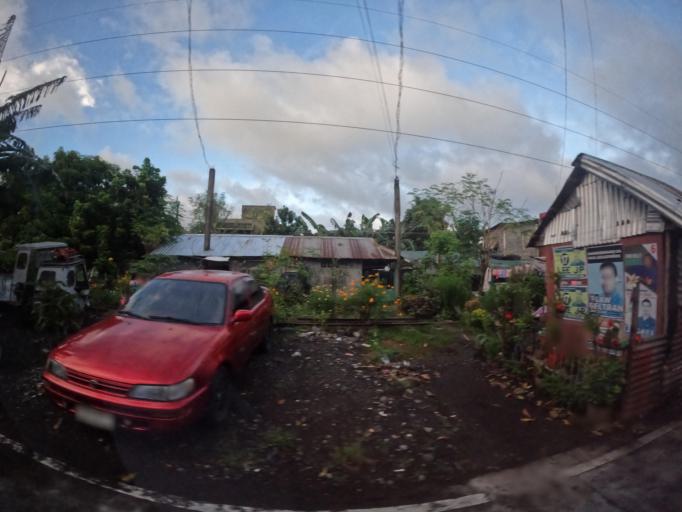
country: PH
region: Bicol
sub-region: Province of Albay
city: Sagpon
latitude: 13.1590
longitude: 123.7390
